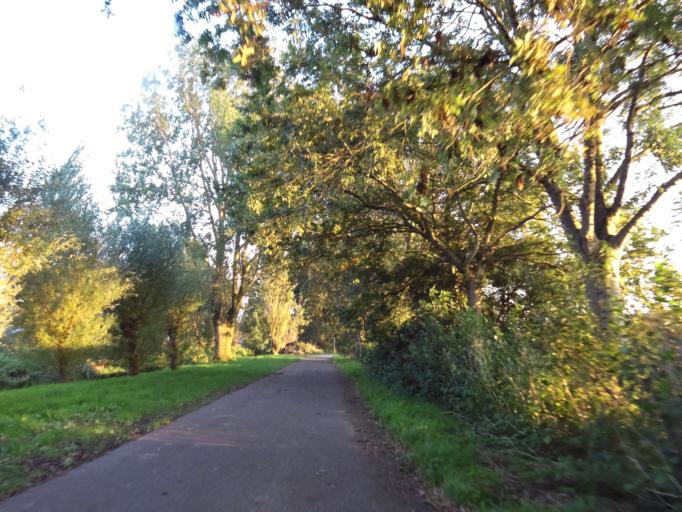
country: NL
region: South Holland
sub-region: Gemeente Alphen aan den Rijn
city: Alphen aan den Rijn
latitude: 52.1362
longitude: 4.5937
